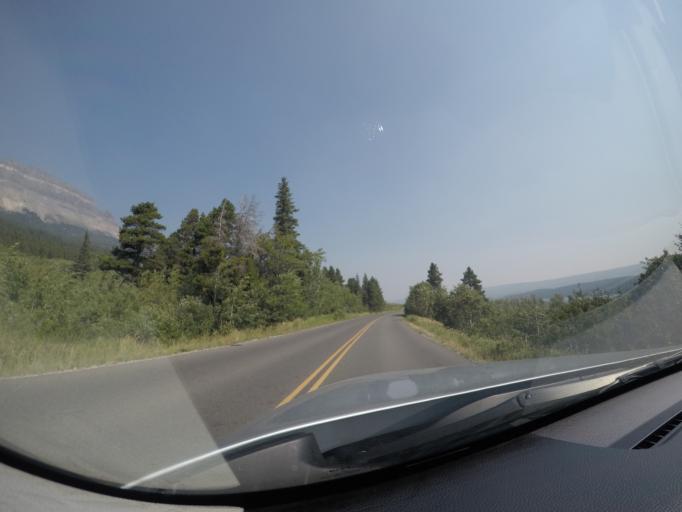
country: US
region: Montana
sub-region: Glacier County
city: North Browning
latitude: 48.7202
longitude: -113.4737
